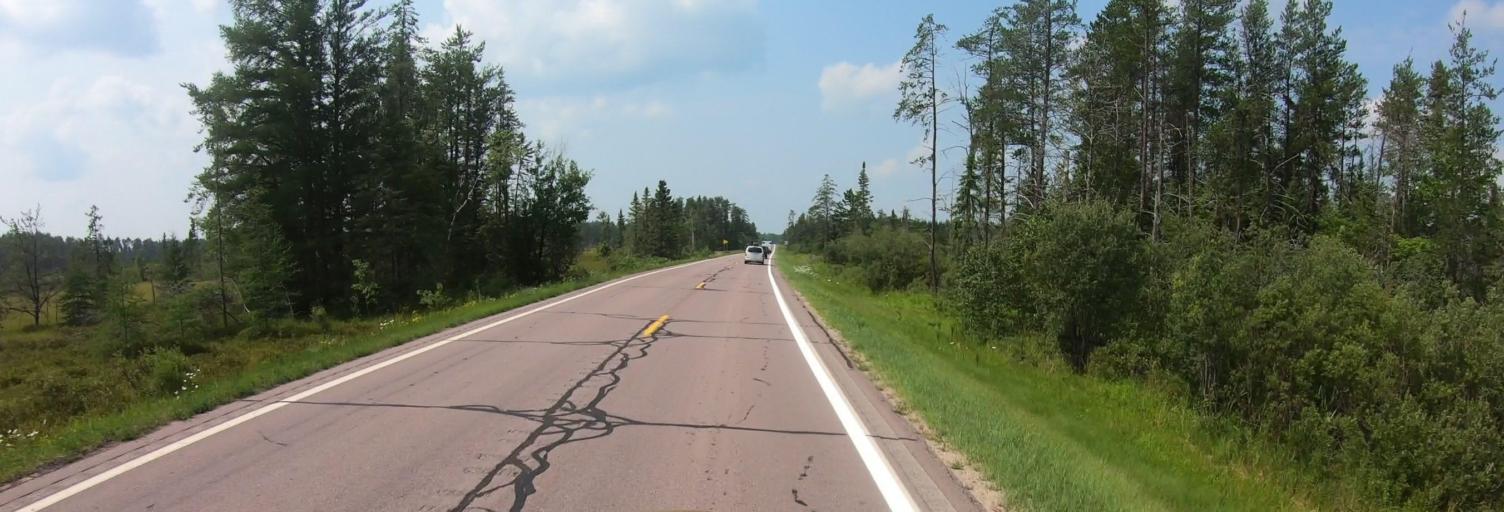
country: US
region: Michigan
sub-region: Luce County
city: Newberry
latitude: 46.4622
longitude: -85.4405
